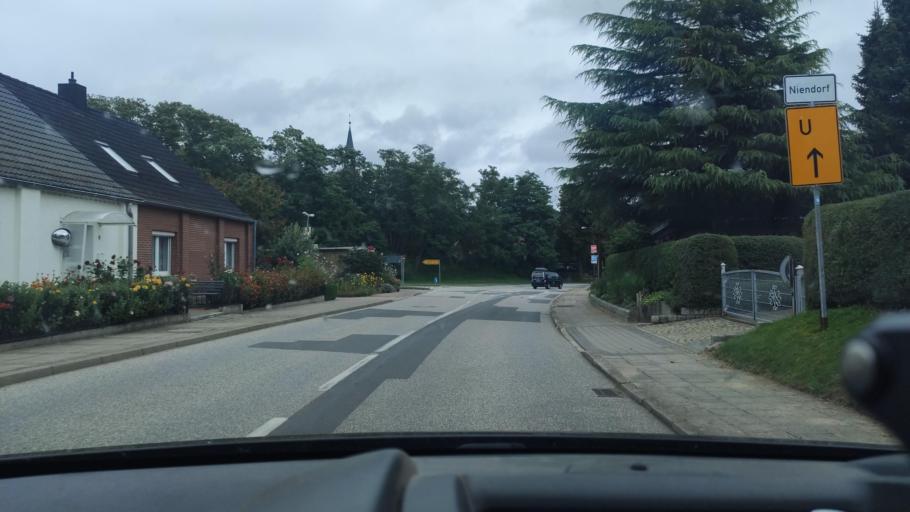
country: DE
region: Mecklenburg-Vorpommern
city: Guestrow
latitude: 53.8389
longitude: 12.1410
